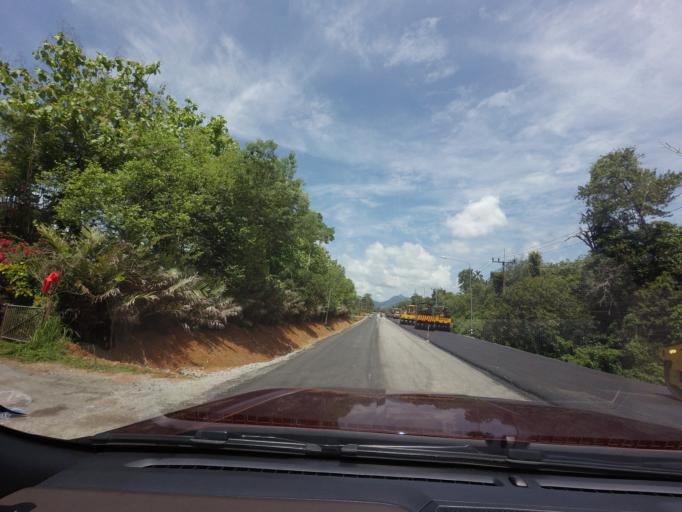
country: TH
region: Narathiwat
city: Ra-ngae
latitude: 6.2876
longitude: 101.7051
